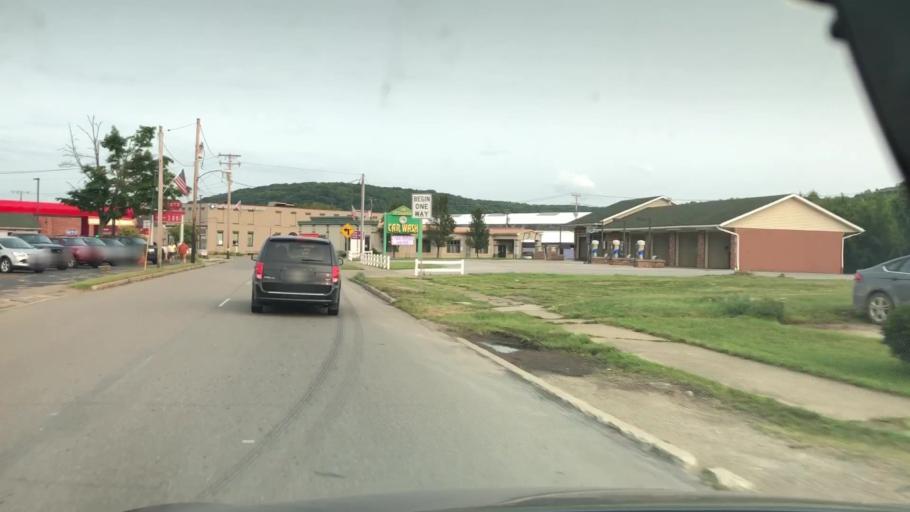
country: US
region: Pennsylvania
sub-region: Crawford County
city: Titusville
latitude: 41.6270
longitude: -79.6806
